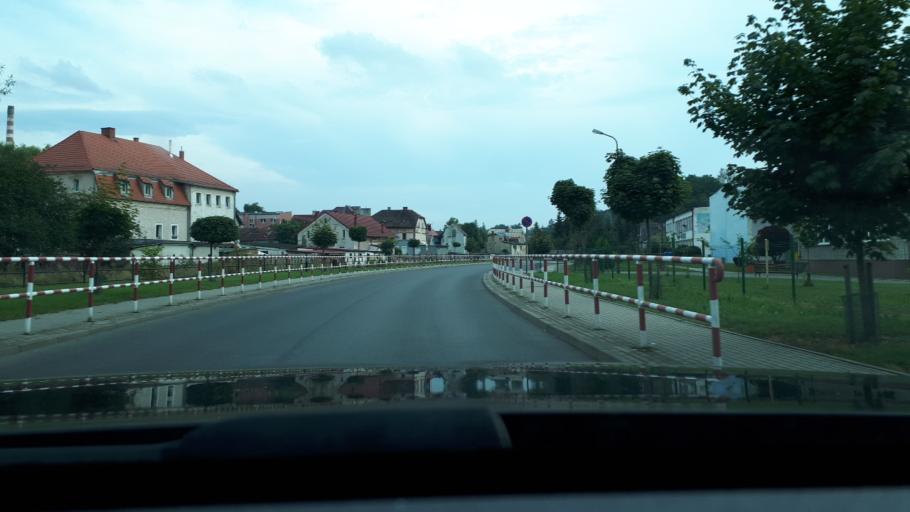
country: PL
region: Lower Silesian Voivodeship
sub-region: Powiat lubanski
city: Lesna
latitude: 51.0232
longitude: 15.2610
